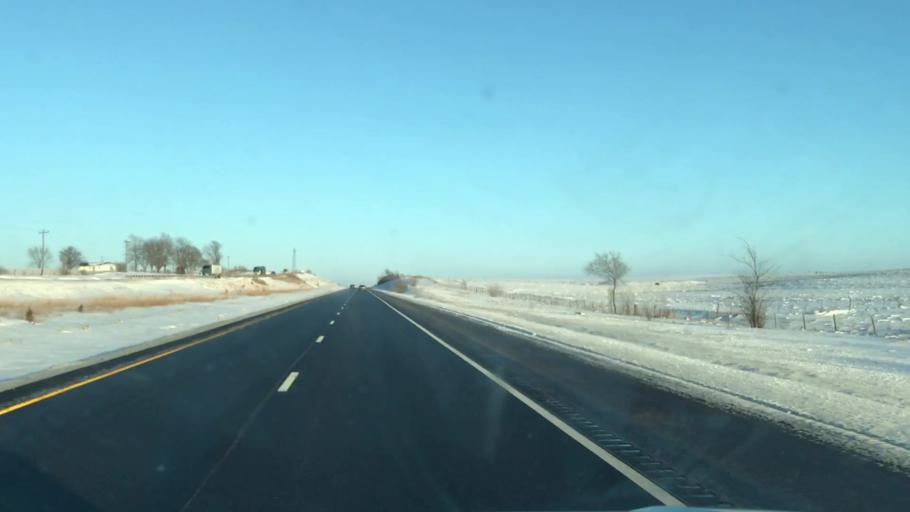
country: US
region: Missouri
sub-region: Clinton County
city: Gower
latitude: 39.7614
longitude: -94.5501
